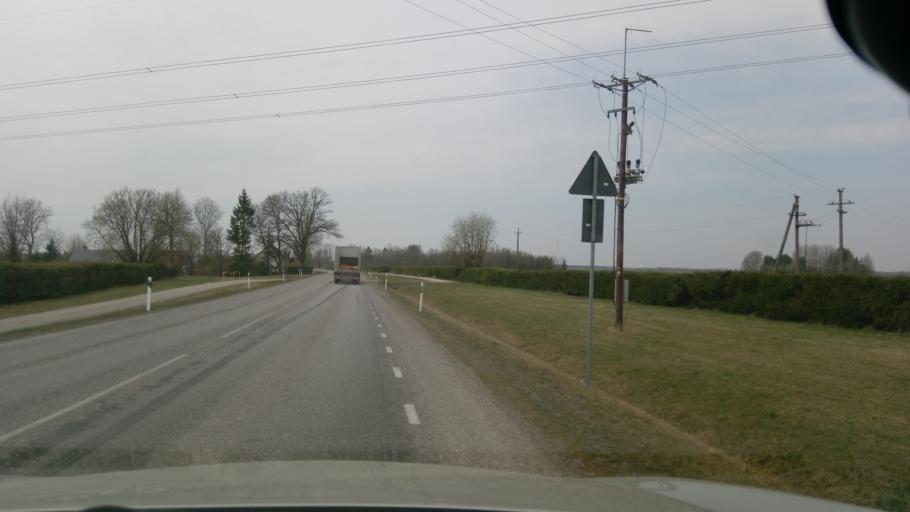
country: EE
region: Jaervamaa
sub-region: Tueri vald
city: Sarevere
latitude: 58.7787
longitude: 25.4630
